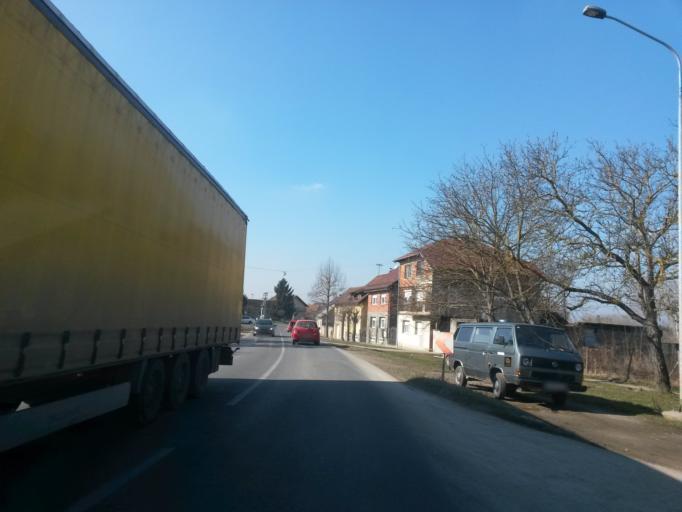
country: HR
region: Osjecko-Baranjska
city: Petrijevci
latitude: 45.6128
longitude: 18.5425
